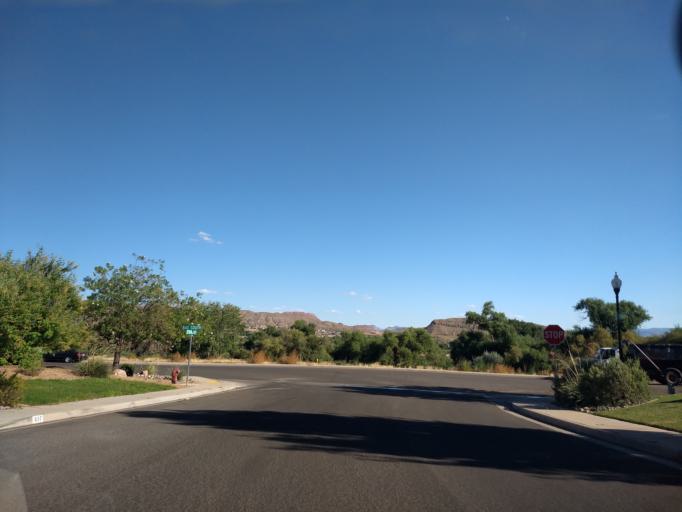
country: US
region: Utah
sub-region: Washington County
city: Washington
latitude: 37.1185
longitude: -113.5050
